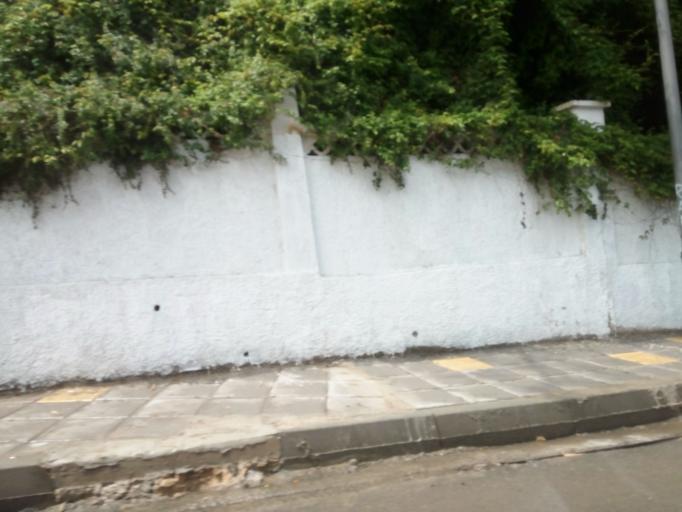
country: DZ
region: Alger
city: Algiers
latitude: 36.7733
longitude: 3.0421
